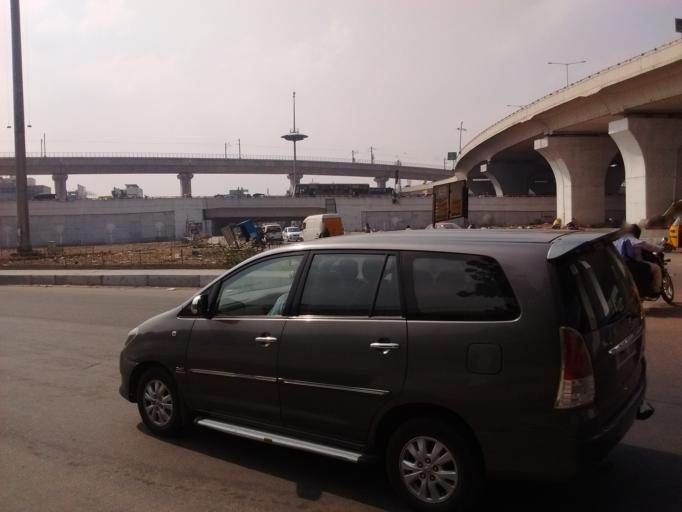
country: IN
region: Tamil Nadu
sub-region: Kancheepuram
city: Alandur
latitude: 13.0085
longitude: 80.2041
